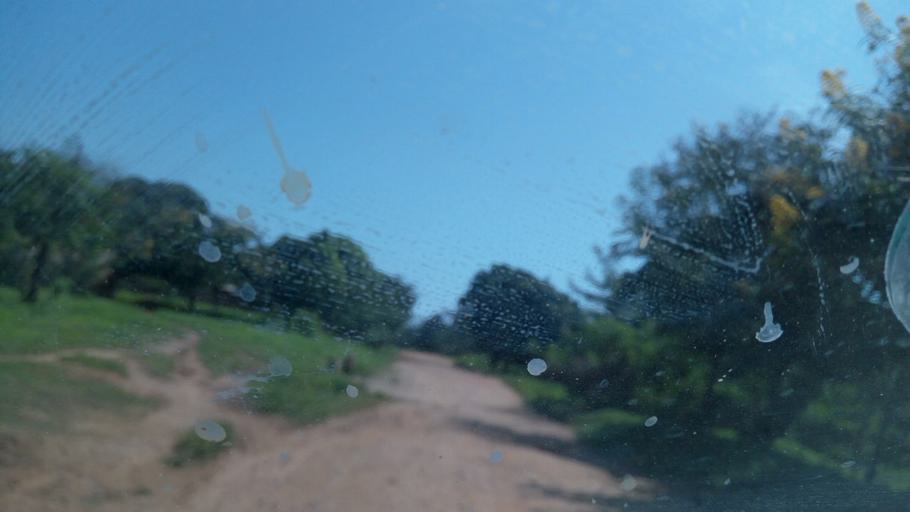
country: CD
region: South Kivu
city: Uvira
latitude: -3.7174
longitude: 29.1184
